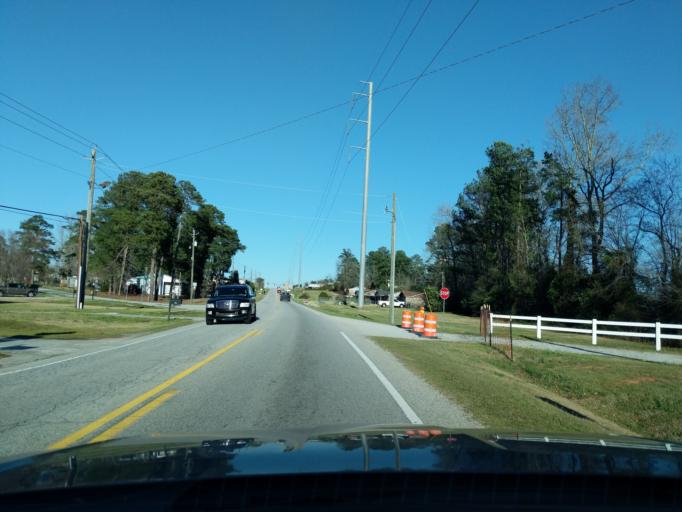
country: US
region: Georgia
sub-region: Columbia County
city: Grovetown
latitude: 33.4519
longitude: -82.2127
